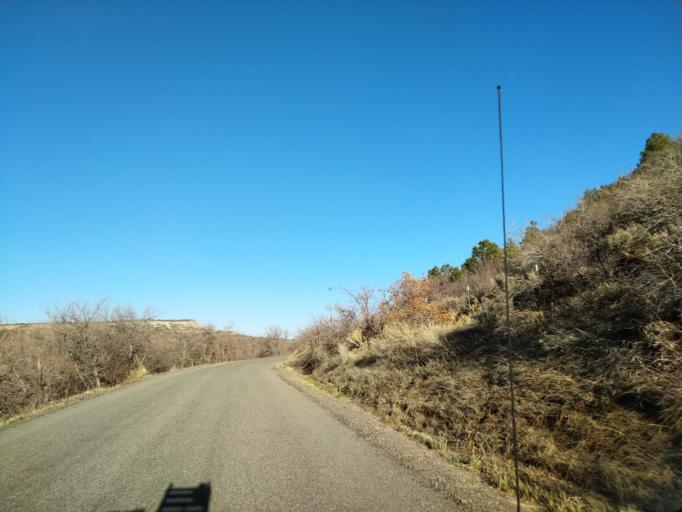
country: US
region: Colorado
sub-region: Mesa County
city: Loma
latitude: 38.9518
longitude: -108.9901
